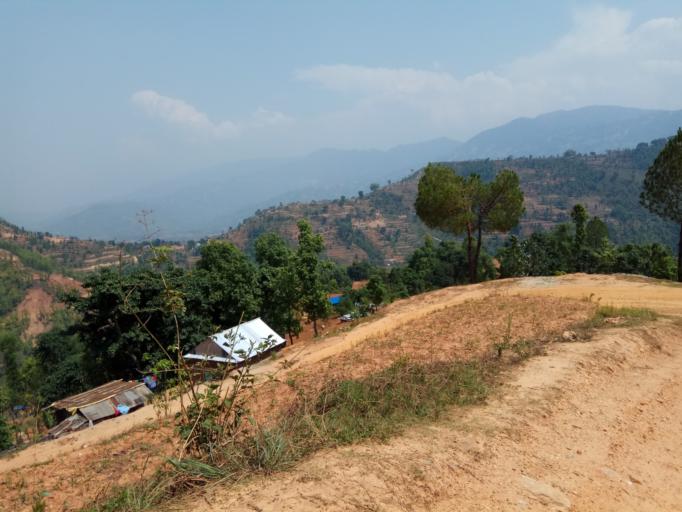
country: NP
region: Central Region
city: Kirtipur
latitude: 27.8910
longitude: 85.0823
